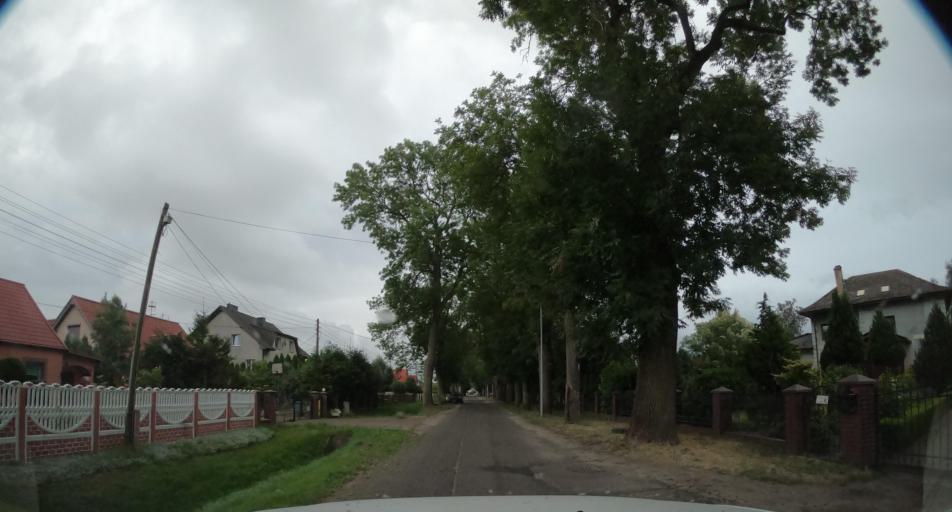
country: PL
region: West Pomeranian Voivodeship
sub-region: Powiat stargardzki
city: Stargard Szczecinski
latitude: 53.3335
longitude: 15.0652
